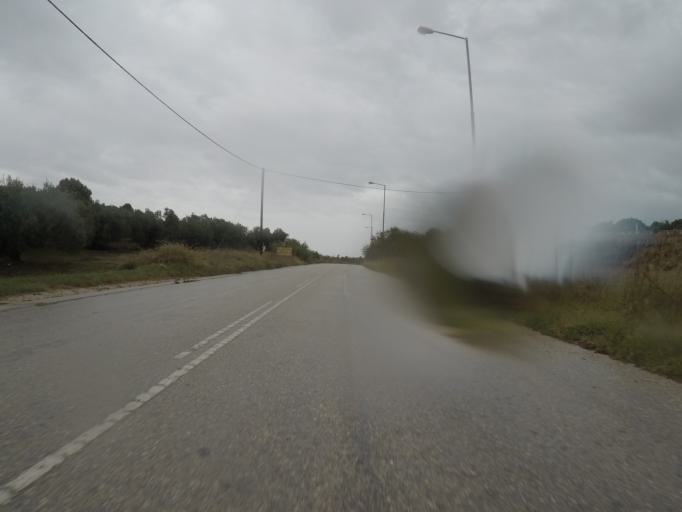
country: GR
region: Peloponnese
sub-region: Nomos Korinthias
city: Arkhaia Korinthos
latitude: 37.8981
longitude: 22.8915
